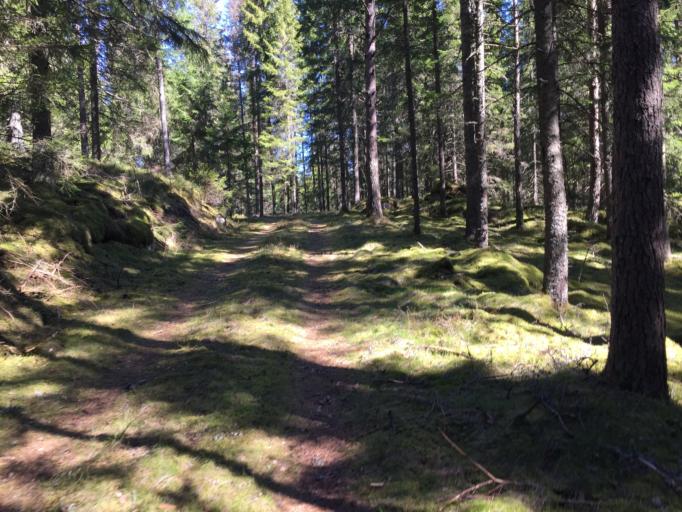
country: SE
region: Joenkoeping
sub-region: Vaggeryds Kommun
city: Skillingaryd
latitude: 57.4655
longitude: 14.0040
